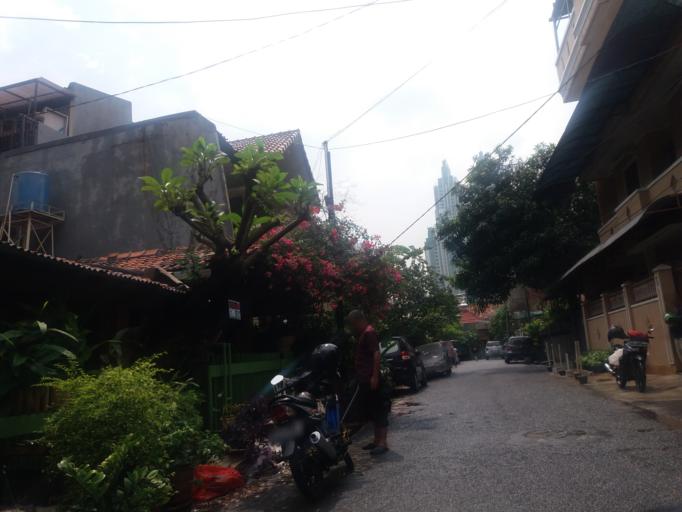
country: ID
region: Jakarta Raya
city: Jakarta
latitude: -6.2152
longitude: 106.8239
